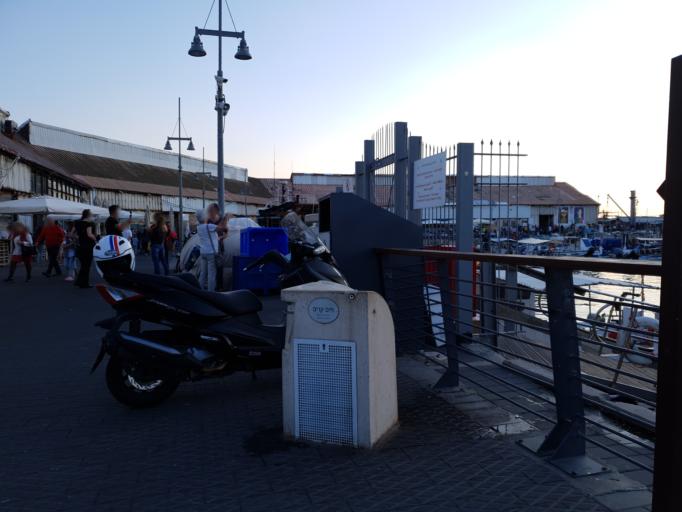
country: IL
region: Tel Aviv
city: Yafo
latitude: 32.0523
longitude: 34.7497
